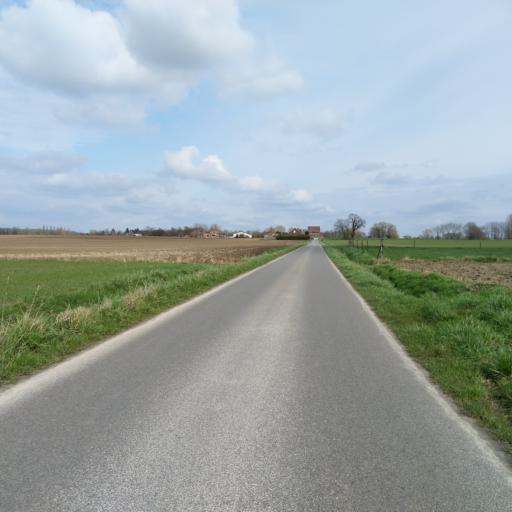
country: BE
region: Wallonia
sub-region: Province du Hainaut
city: Soignies
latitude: 50.5462
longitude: 4.0310
